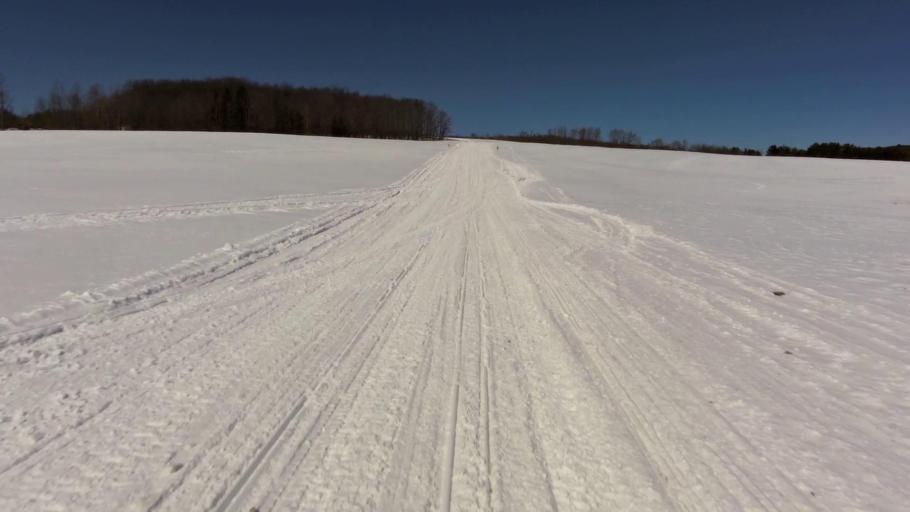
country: US
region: New York
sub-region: Allegany County
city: Houghton
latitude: 42.3963
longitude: -78.2596
